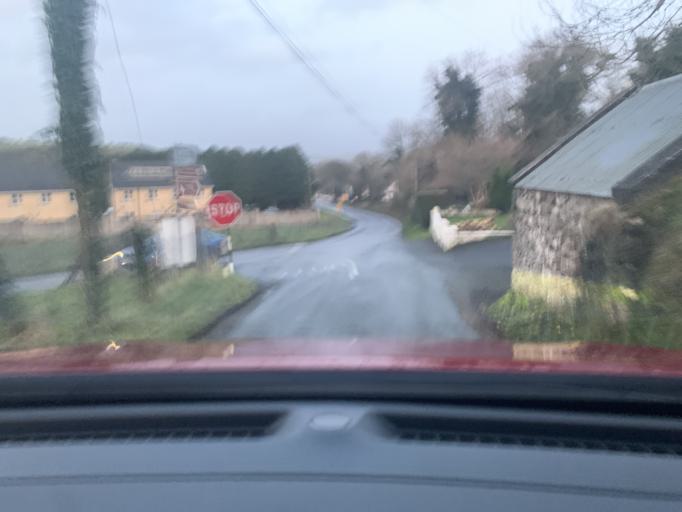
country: IE
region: Connaught
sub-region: Sligo
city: Ballymote
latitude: 54.0770
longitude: -8.3815
